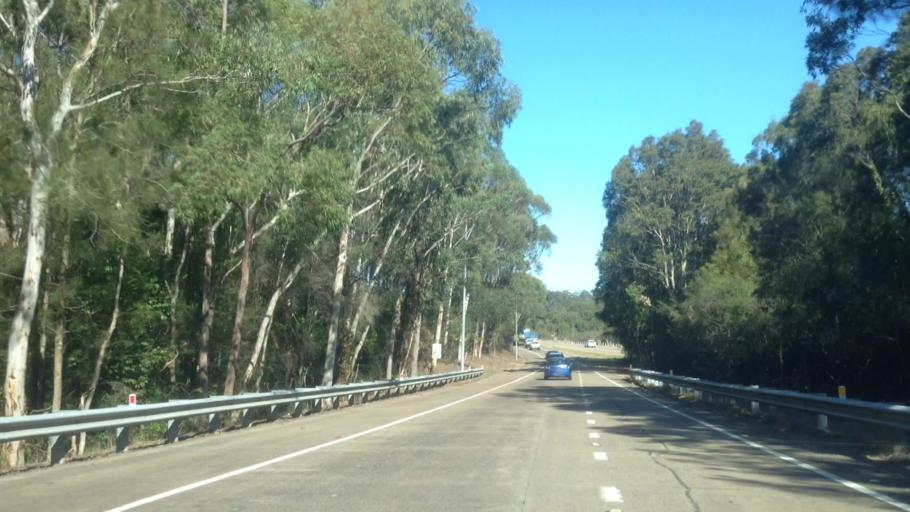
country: AU
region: New South Wales
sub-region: Lake Macquarie Shire
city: Cooranbong
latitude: -33.1193
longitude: 151.4668
